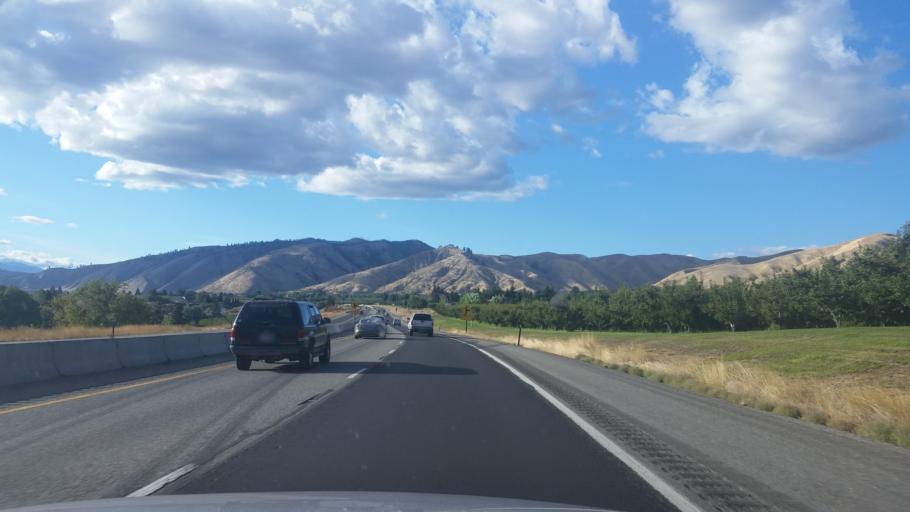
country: US
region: Washington
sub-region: Chelan County
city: Cashmere
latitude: 47.4985
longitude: -120.4215
